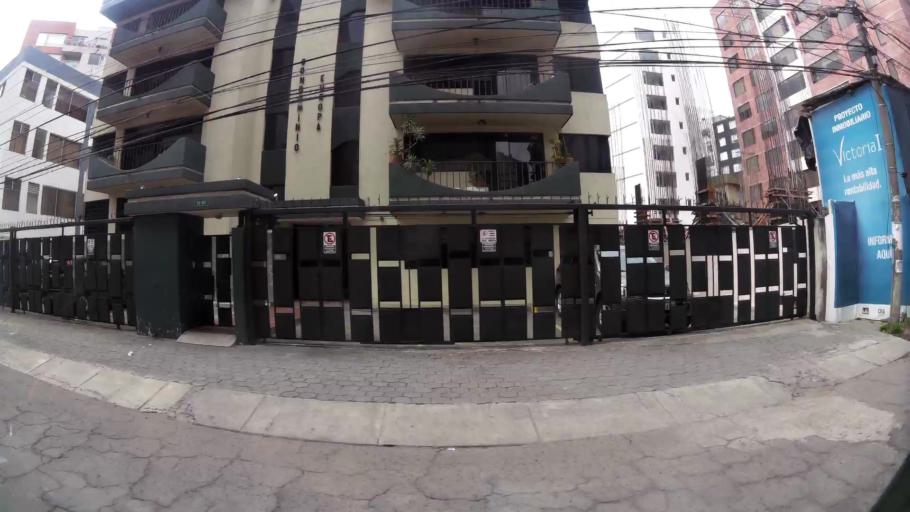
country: EC
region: Pichincha
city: Quito
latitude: -0.1859
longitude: -78.4807
